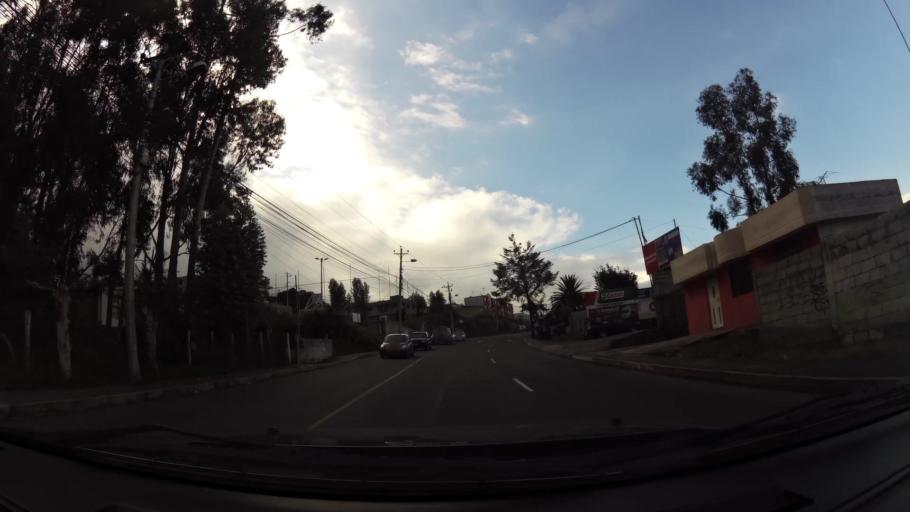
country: EC
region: Pichincha
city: Sangolqui
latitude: -0.2860
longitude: -78.4892
